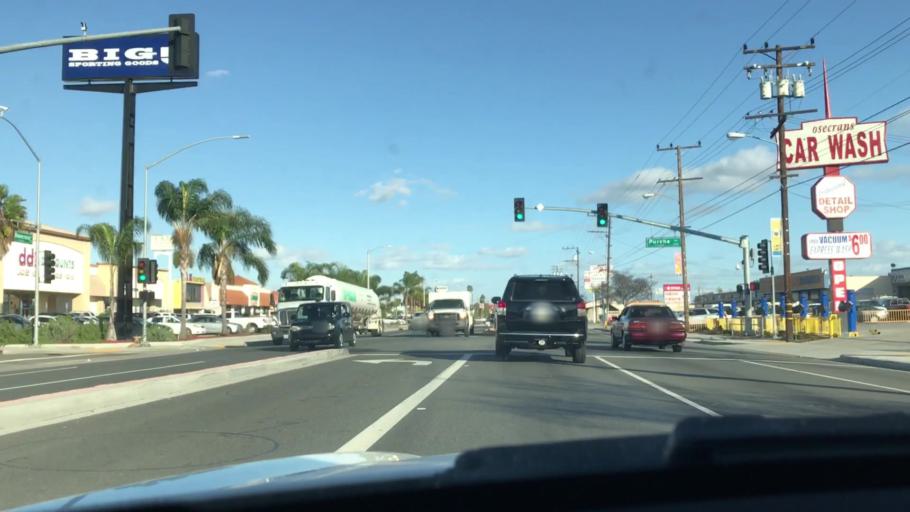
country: US
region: California
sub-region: Los Angeles County
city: Alondra Park
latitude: 33.9019
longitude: -118.3209
